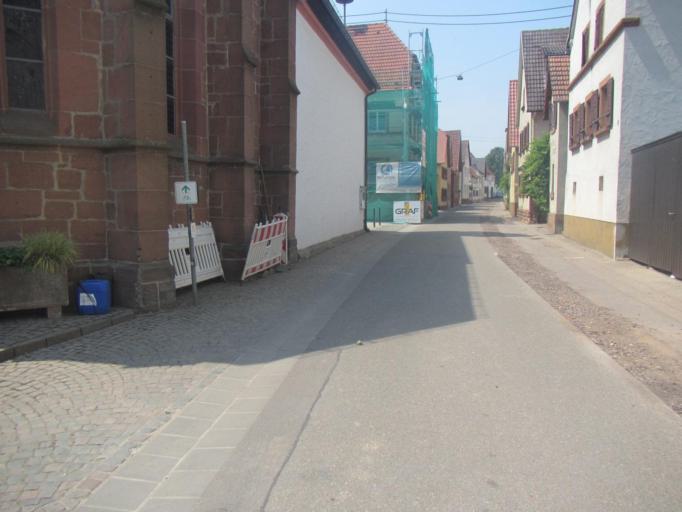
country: DE
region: Rheinland-Pfalz
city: Niederhorbach
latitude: 49.1159
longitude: 8.0322
